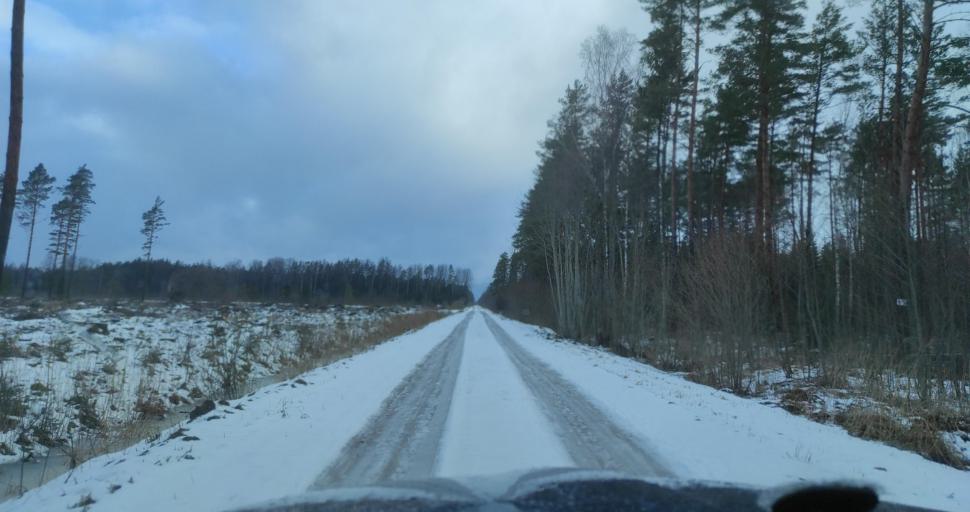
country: LV
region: Dundaga
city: Dundaga
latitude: 57.4022
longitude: 22.1033
